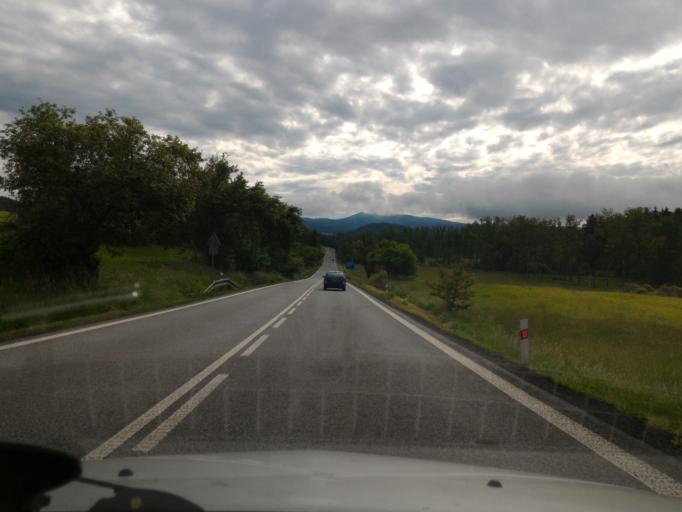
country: CZ
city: Jablonne v Podjestedi
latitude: 50.7865
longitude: 14.8005
